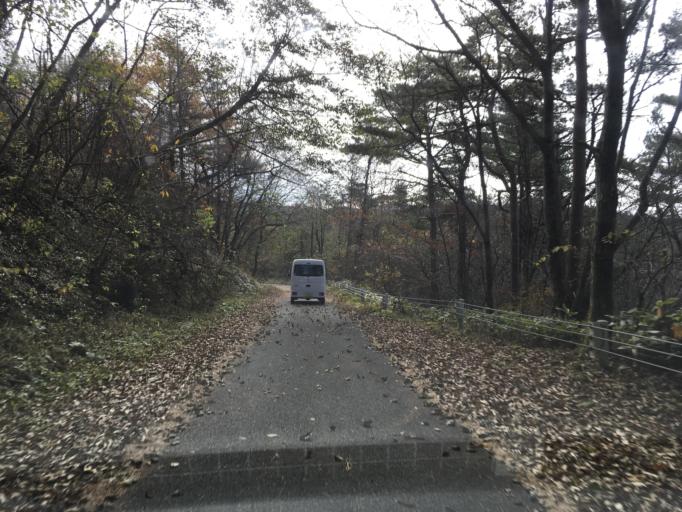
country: JP
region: Iwate
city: Mizusawa
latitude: 39.1238
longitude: 141.3020
